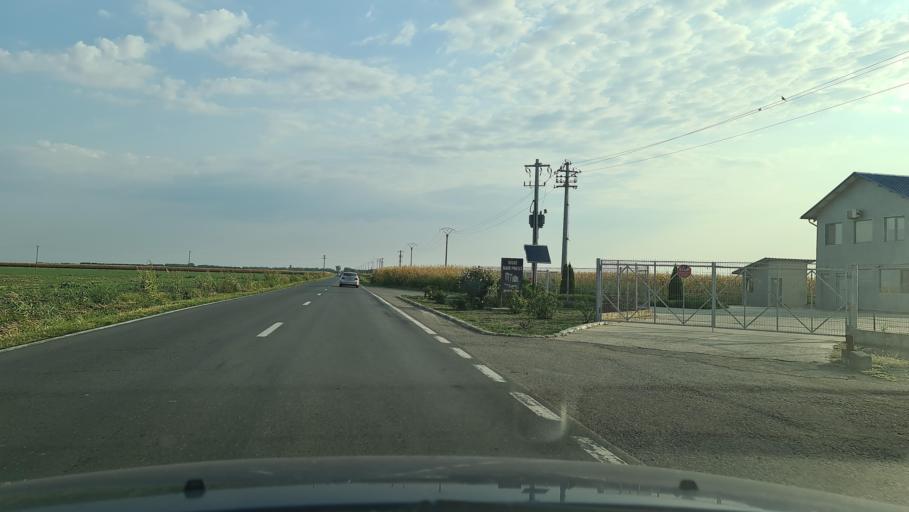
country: RO
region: Calarasi
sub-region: Oras Lehliu Gara
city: Razvani
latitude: 44.4416
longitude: 26.8925
